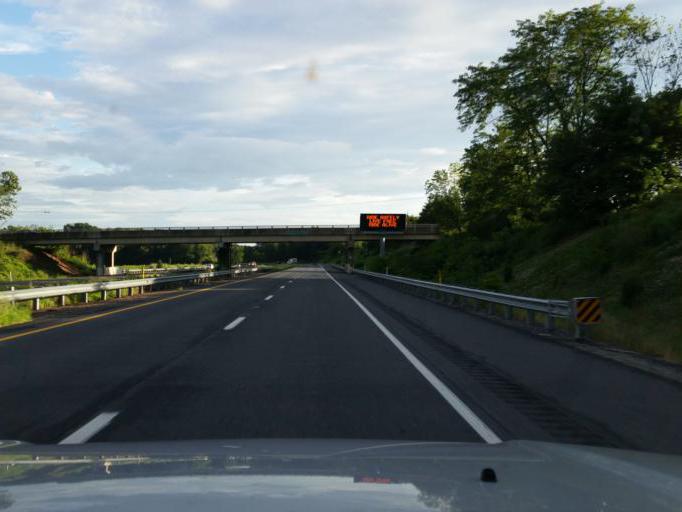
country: US
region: Pennsylvania
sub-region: Adams County
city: Lake Meade
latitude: 39.9806
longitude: -77.1251
